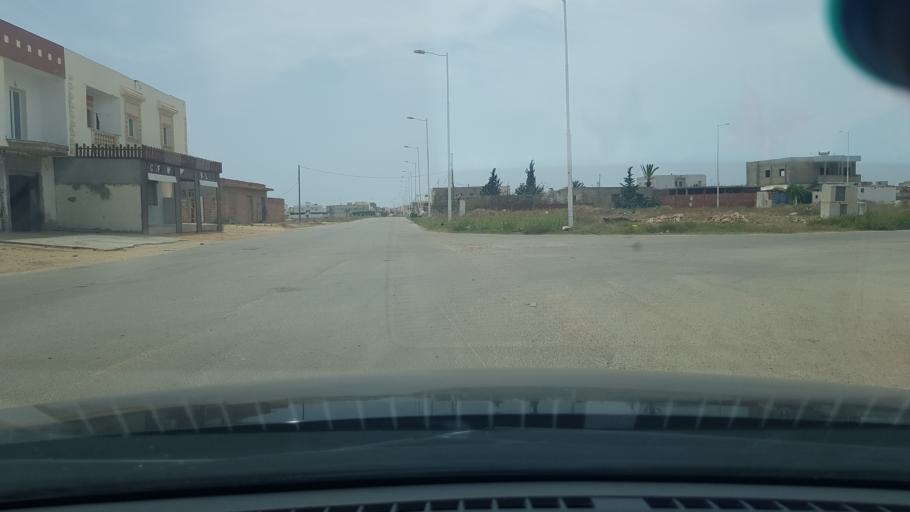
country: TN
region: Safaqis
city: Al Qarmadah
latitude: 34.8303
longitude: 10.7491
